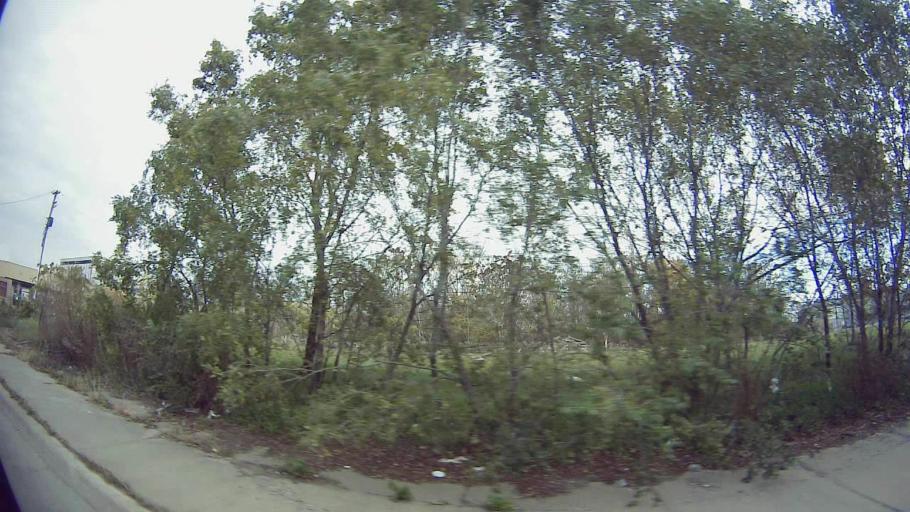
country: US
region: Michigan
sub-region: Wayne County
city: Hamtramck
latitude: 42.3649
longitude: -83.0526
